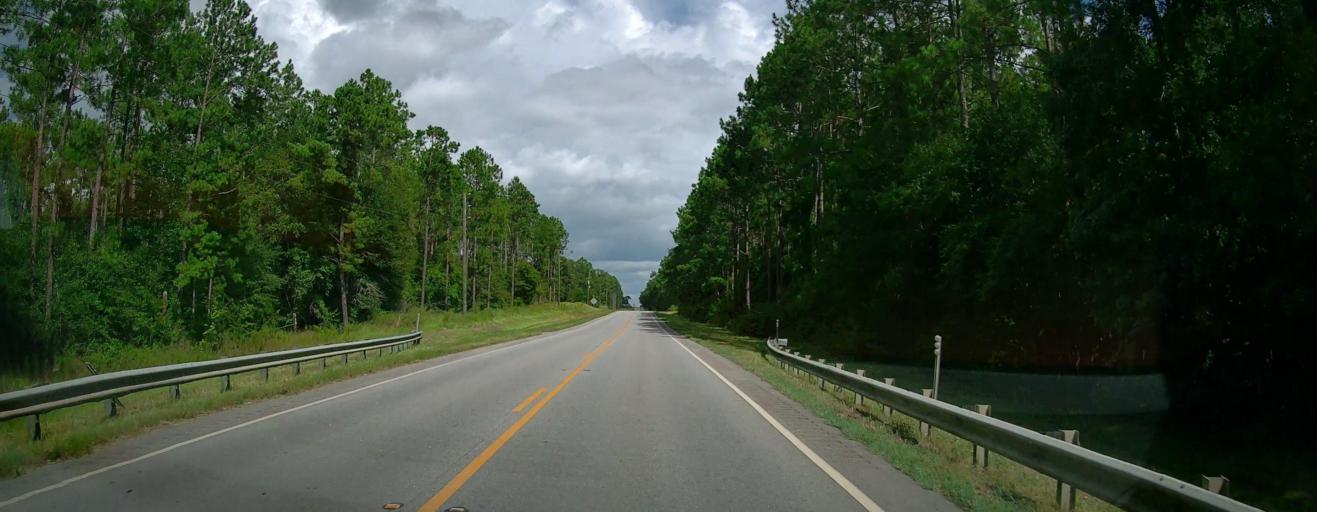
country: US
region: Georgia
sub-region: Coffee County
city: Broxton
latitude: 31.5747
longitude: -83.0394
